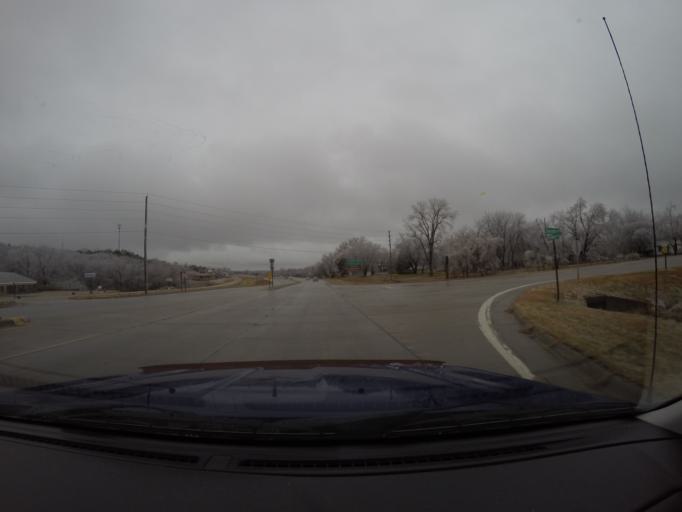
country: US
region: Kansas
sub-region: Riley County
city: Manhattan
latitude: 39.1725
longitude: -96.5464
